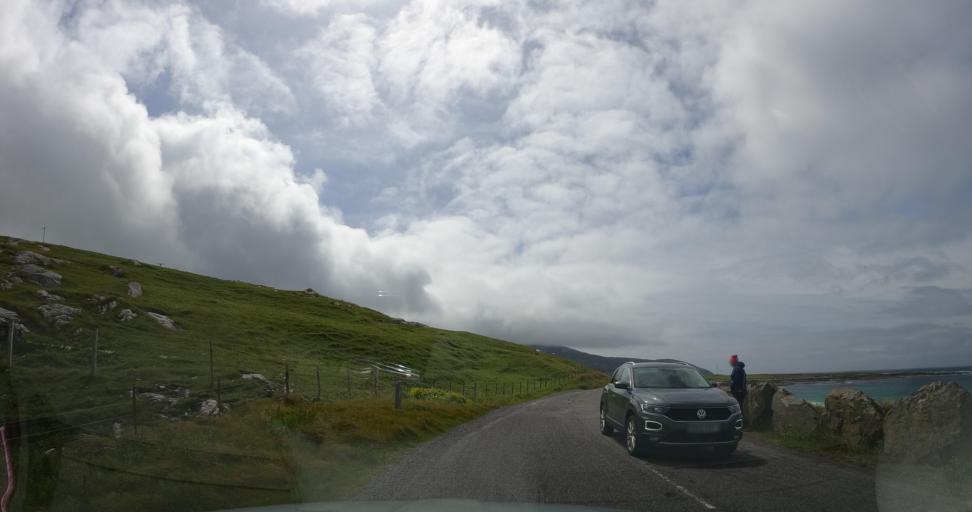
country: GB
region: Scotland
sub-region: Eilean Siar
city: Barra
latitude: 56.9910
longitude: -7.5088
